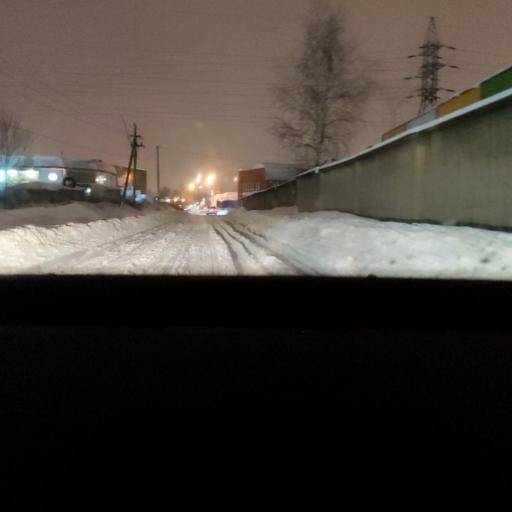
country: RU
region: Moskovskaya
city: Odintsovo
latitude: 55.6614
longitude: 37.2669
